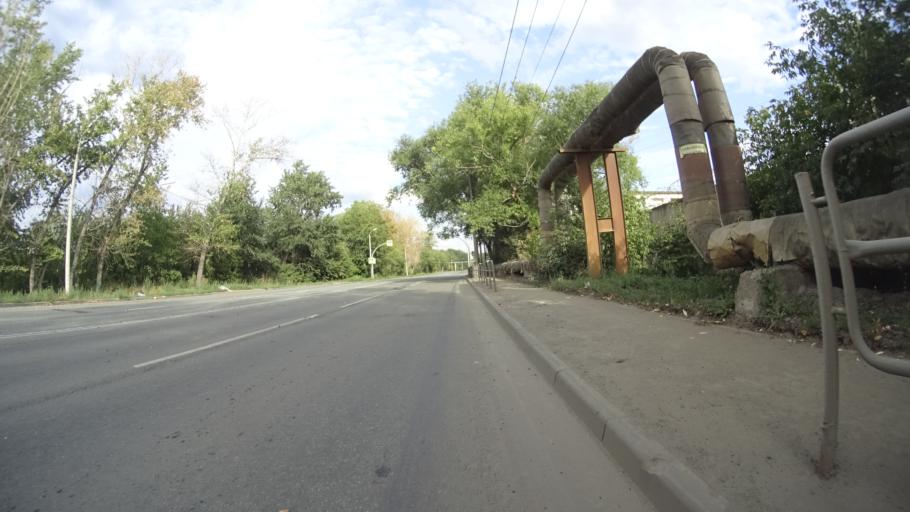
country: RU
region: Chelyabinsk
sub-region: Gorod Chelyabinsk
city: Chelyabinsk
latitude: 55.1959
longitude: 61.3779
